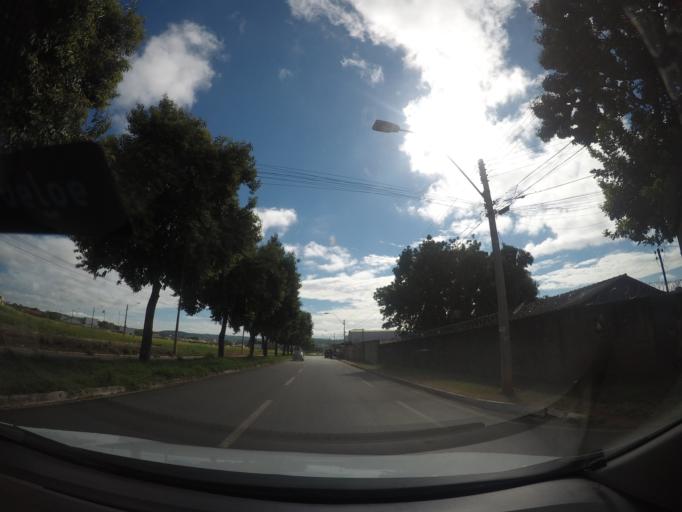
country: BR
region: Goias
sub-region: Goiania
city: Goiania
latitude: -16.6549
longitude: -49.1773
